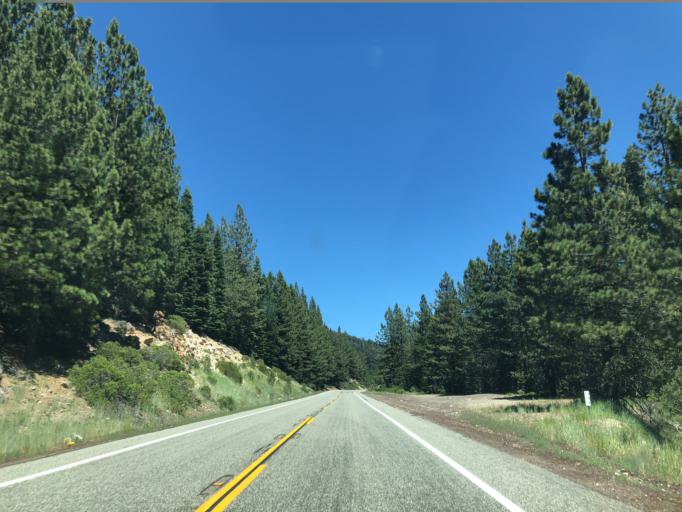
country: US
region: California
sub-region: Shasta County
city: Shingletown
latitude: 40.5409
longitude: -121.5858
